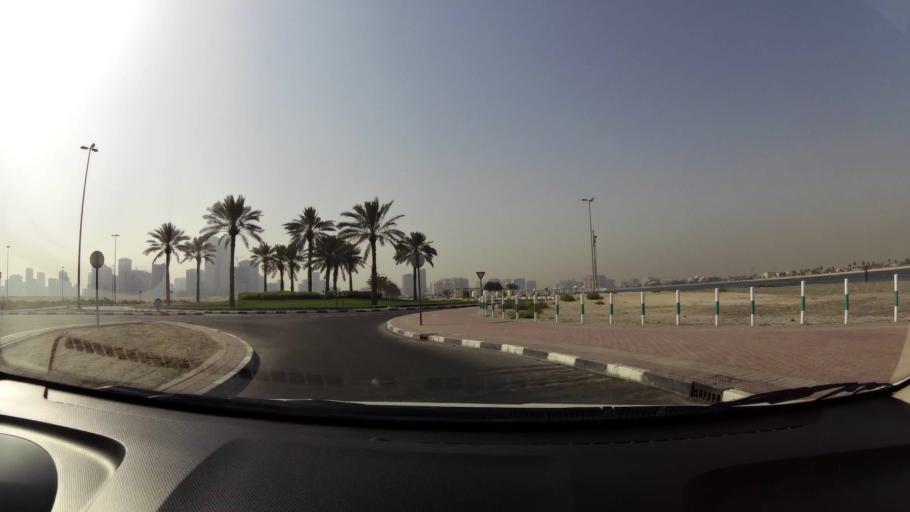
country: AE
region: Ash Shariqah
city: Sharjah
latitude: 25.3103
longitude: 55.3509
